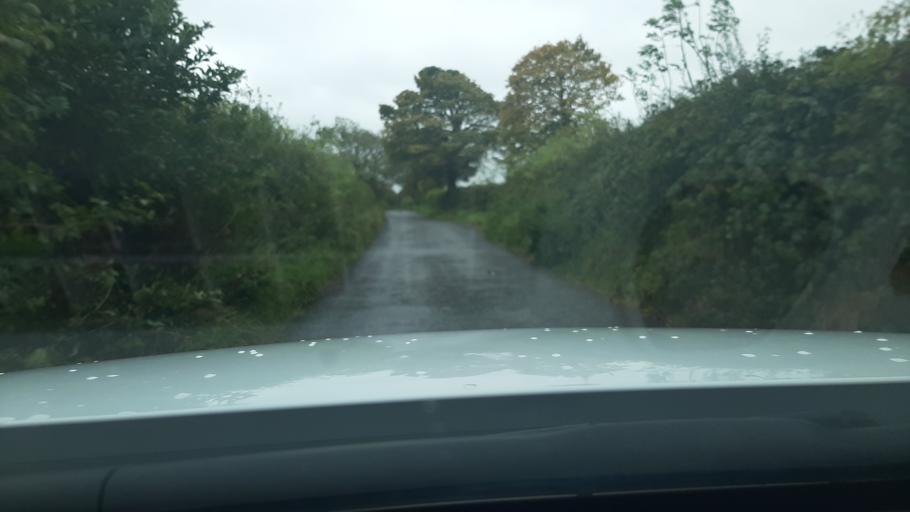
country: IE
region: Leinster
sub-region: Kildare
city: Kildare
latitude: 53.1768
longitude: -6.9252
